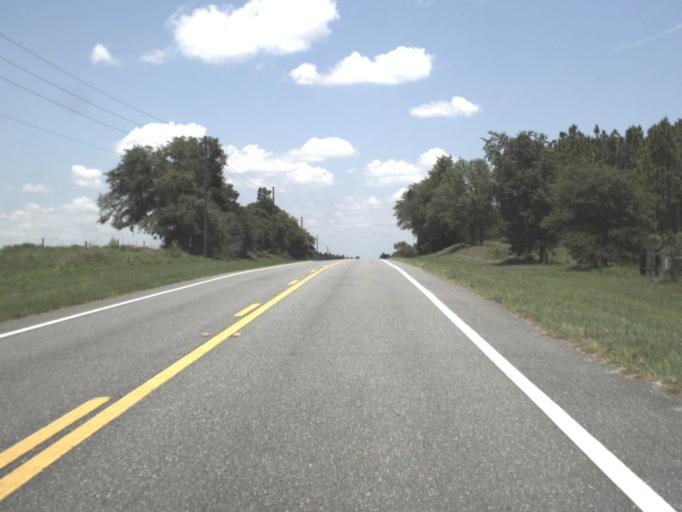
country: US
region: Florida
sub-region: Levy County
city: Williston Highlands
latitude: 29.2528
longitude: -82.5518
